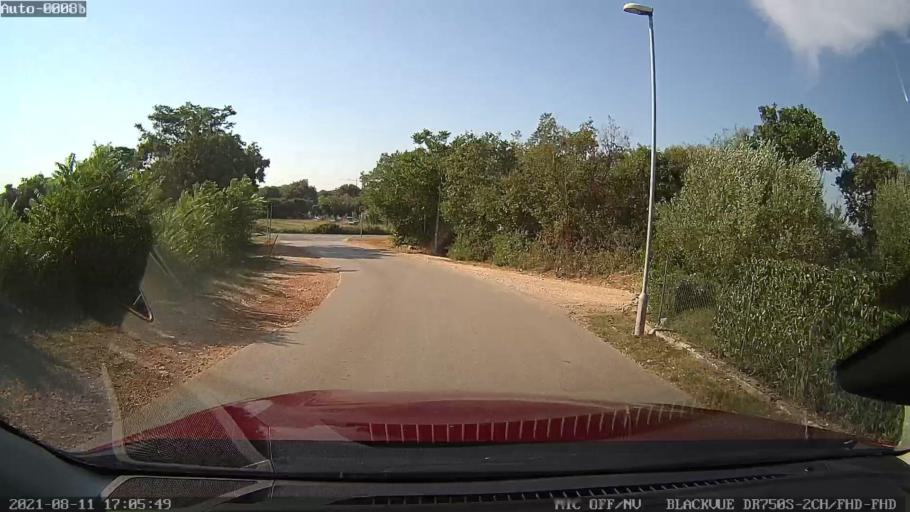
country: HR
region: Istarska
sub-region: Grad Rovinj
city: Rovinj
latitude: 45.0837
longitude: 13.6641
